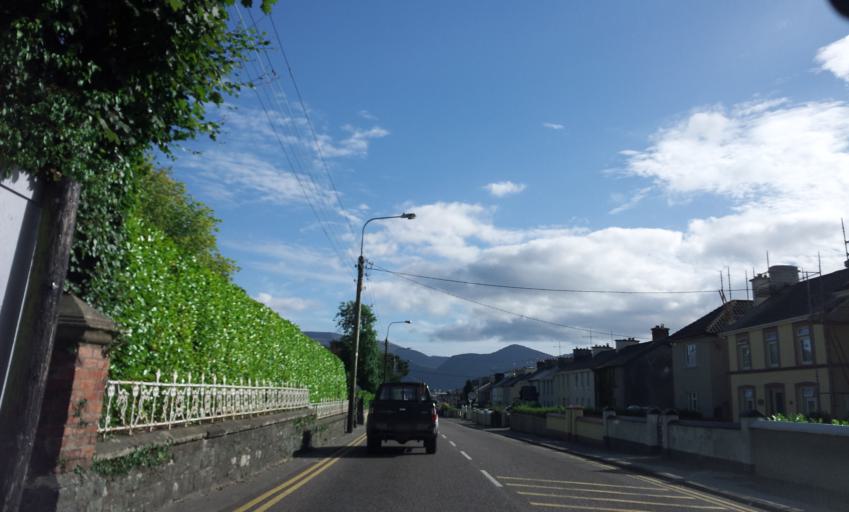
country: IE
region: Munster
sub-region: Ciarrai
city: Cill Airne
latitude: 52.0633
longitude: -9.5061
